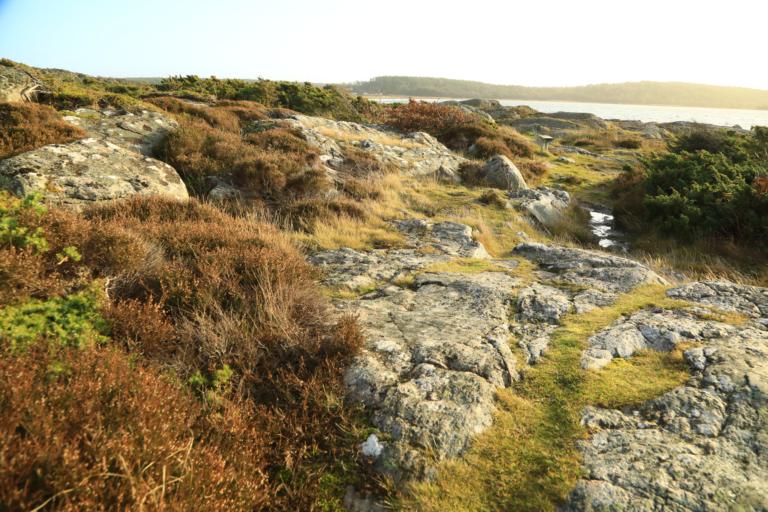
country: SE
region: Halland
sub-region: Varbergs Kommun
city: Varberg
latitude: 57.1876
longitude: 12.2056
